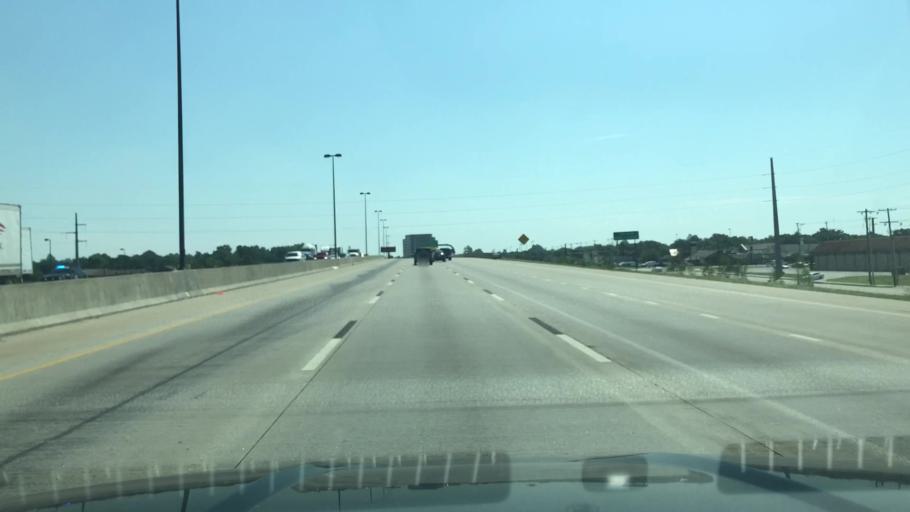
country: US
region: Oklahoma
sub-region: Tulsa County
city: Jenks
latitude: 36.0903
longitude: -95.9433
